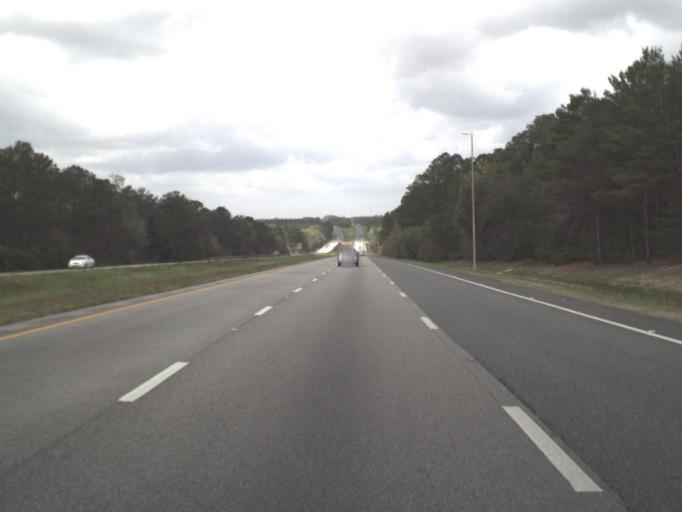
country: US
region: Florida
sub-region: Okaloosa County
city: Crestview
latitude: 30.7271
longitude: -86.5124
